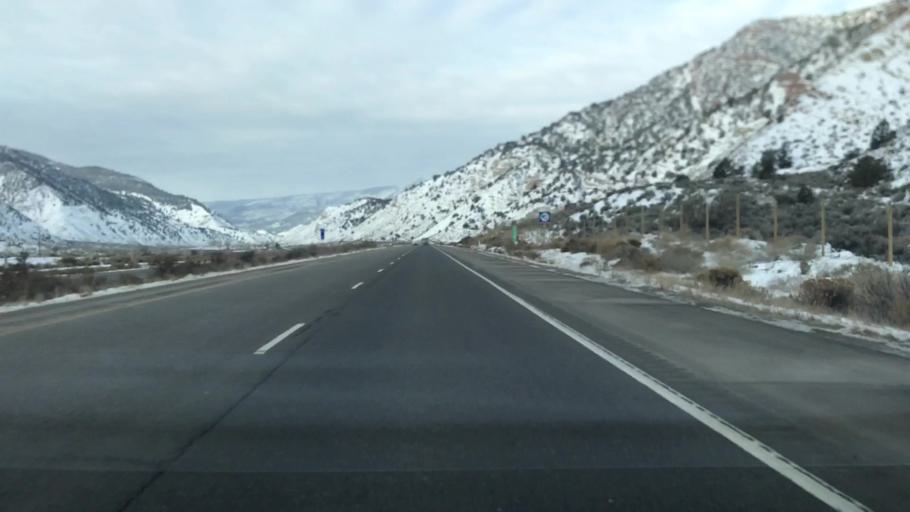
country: US
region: Colorado
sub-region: Eagle County
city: Gypsum
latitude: 39.6491
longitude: -106.9990
